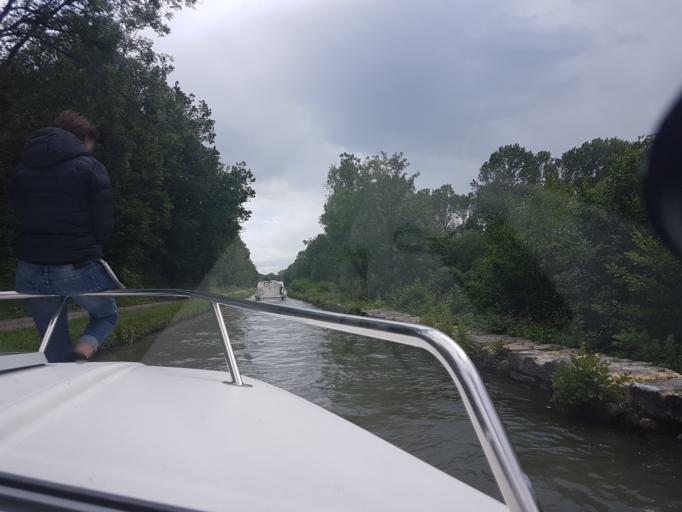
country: FR
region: Bourgogne
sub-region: Departement de l'Yonne
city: Vermenton
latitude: 47.5553
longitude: 3.6334
